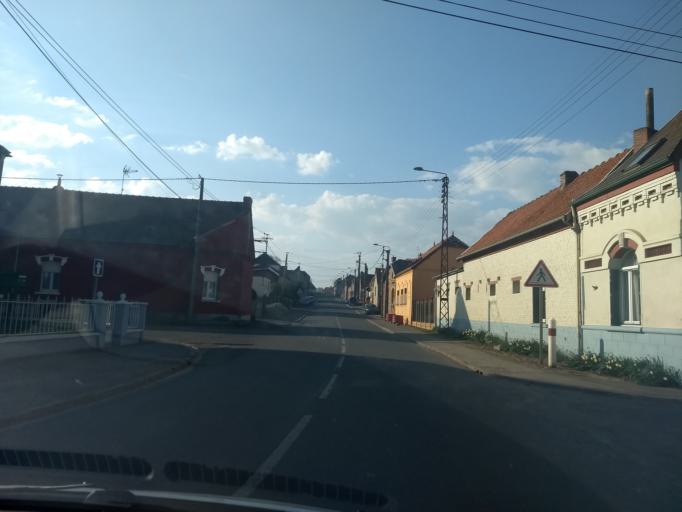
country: FR
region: Nord-Pas-de-Calais
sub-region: Departement du Pas-de-Calais
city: Bucquoy
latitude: 50.1159
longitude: 2.6922
